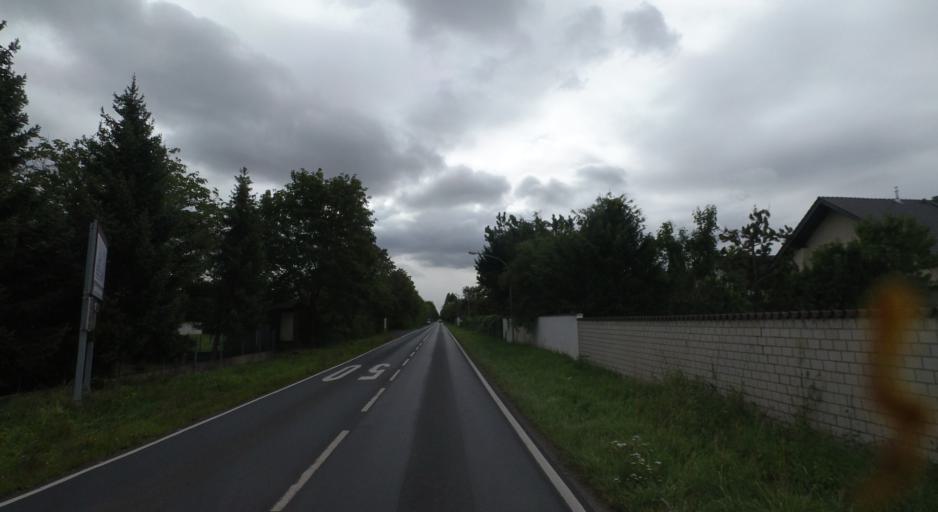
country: DE
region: Hesse
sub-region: Regierungsbezirk Darmstadt
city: Seligenstadt
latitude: 50.0358
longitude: 8.9833
